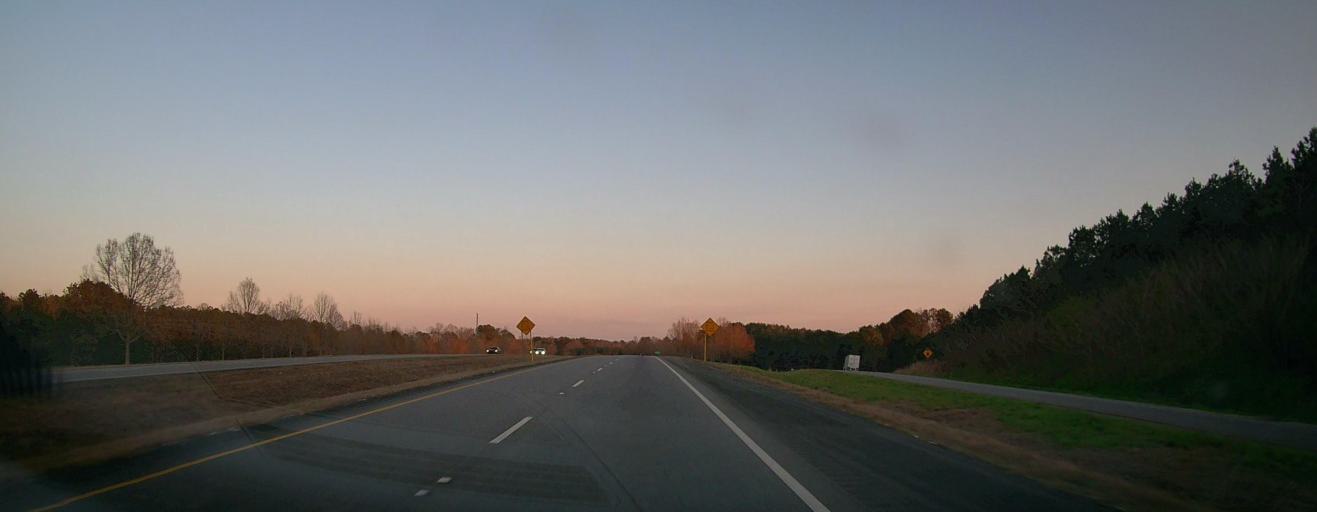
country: US
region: Alabama
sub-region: Coosa County
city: Goodwater
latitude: 32.9873
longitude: -86.0680
